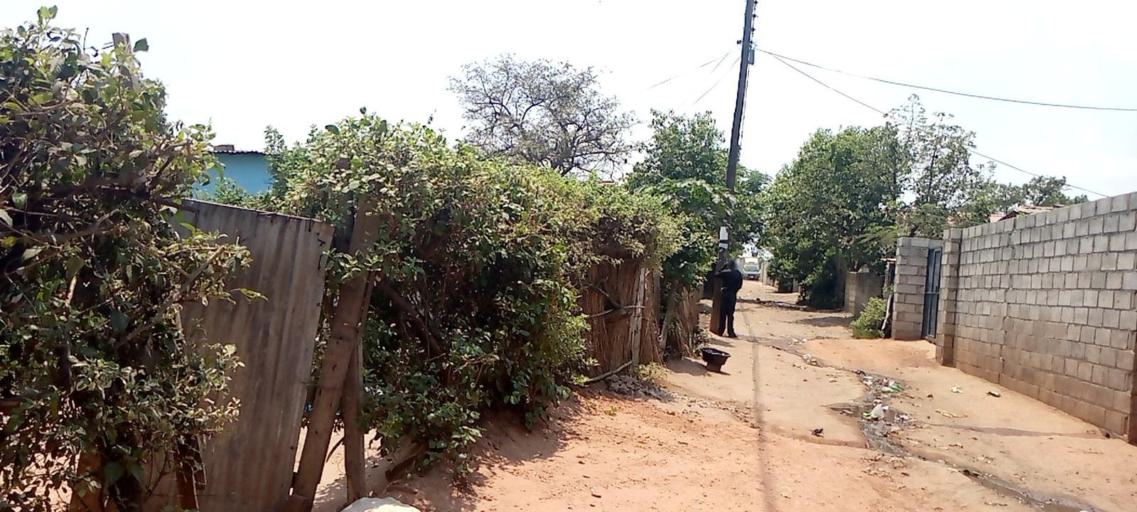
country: ZM
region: Lusaka
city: Lusaka
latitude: -15.4003
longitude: 28.3474
